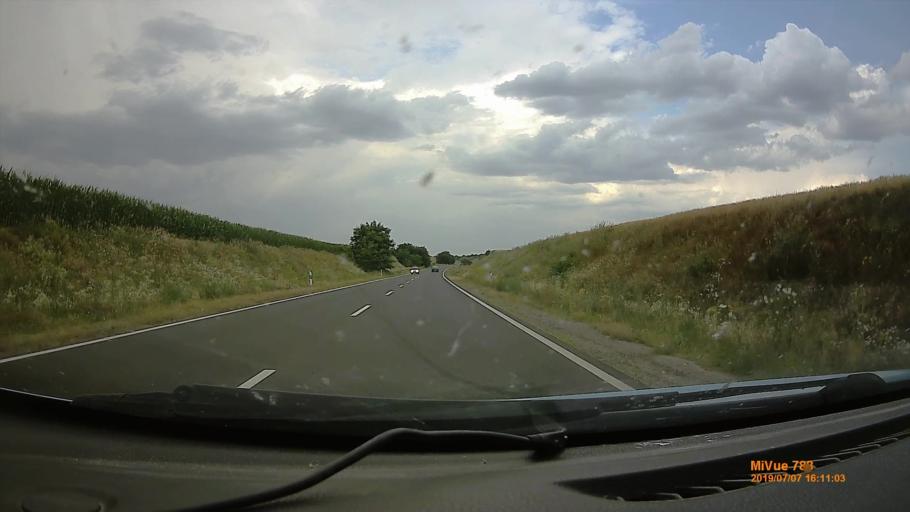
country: HU
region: Heves
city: Hatvan
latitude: 47.6719
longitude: 19.7177
